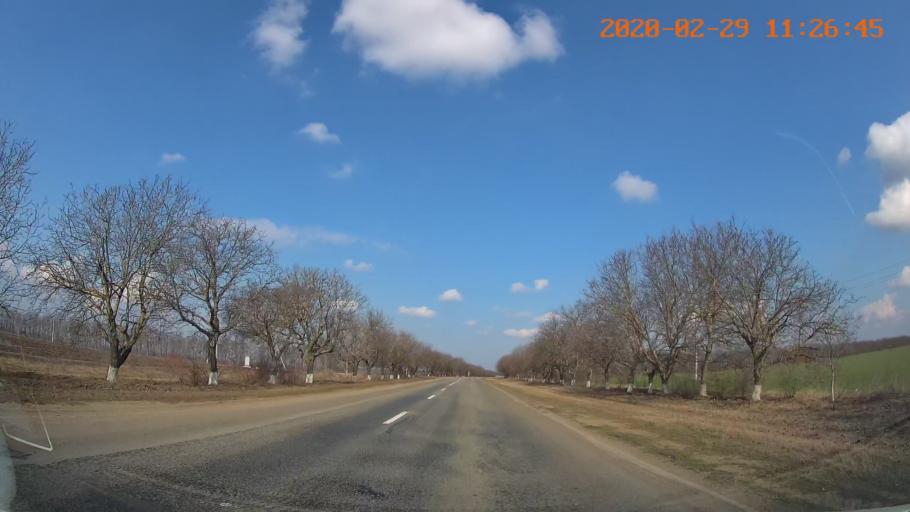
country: MD
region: Telenesti
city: Cocieri
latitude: 47.4575
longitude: 29.1448
